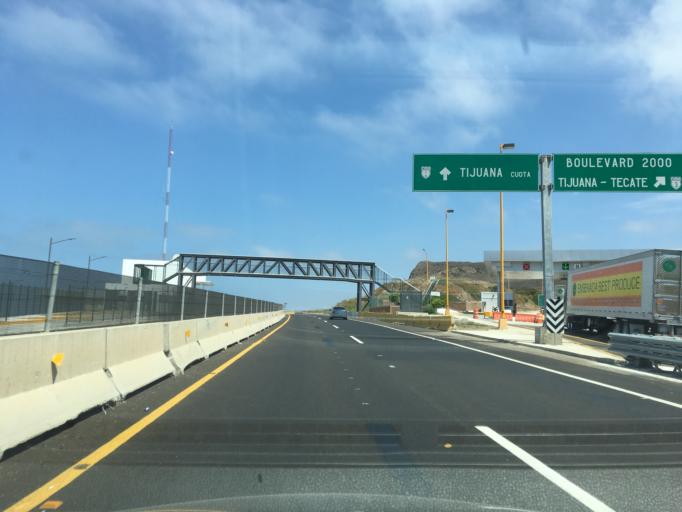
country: MX
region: Baja California
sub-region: Playas de Rosarito
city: Ciudad Morelos
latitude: 32.2827
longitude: -117.0295
